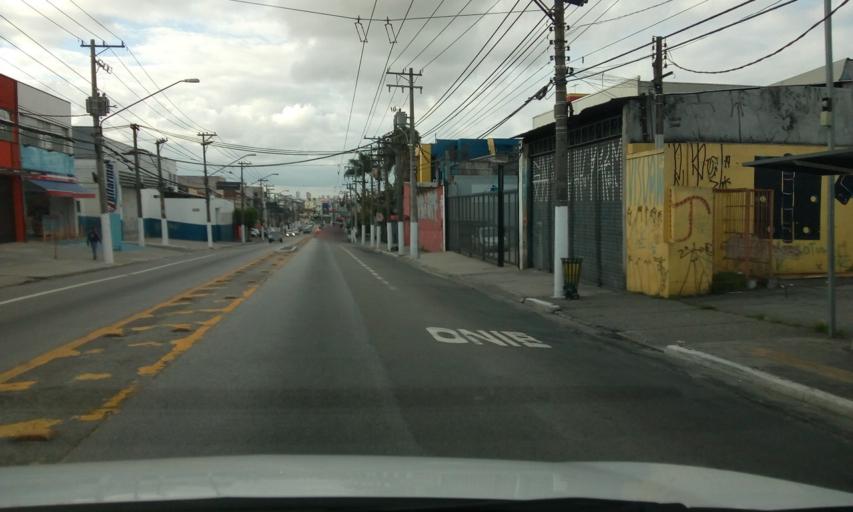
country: BR
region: Sao Paulo
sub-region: Sao Caetano Do Sul
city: Sao Caetano do Sul
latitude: -23.5744
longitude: -46.5048
